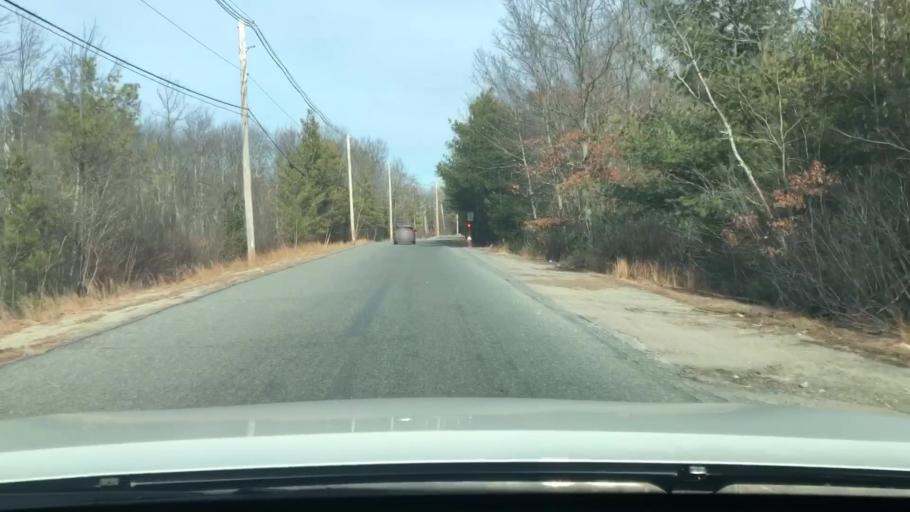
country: US
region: Massachusetts
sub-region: Worcester County
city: Milford
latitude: 42.1435
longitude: -71.4877
